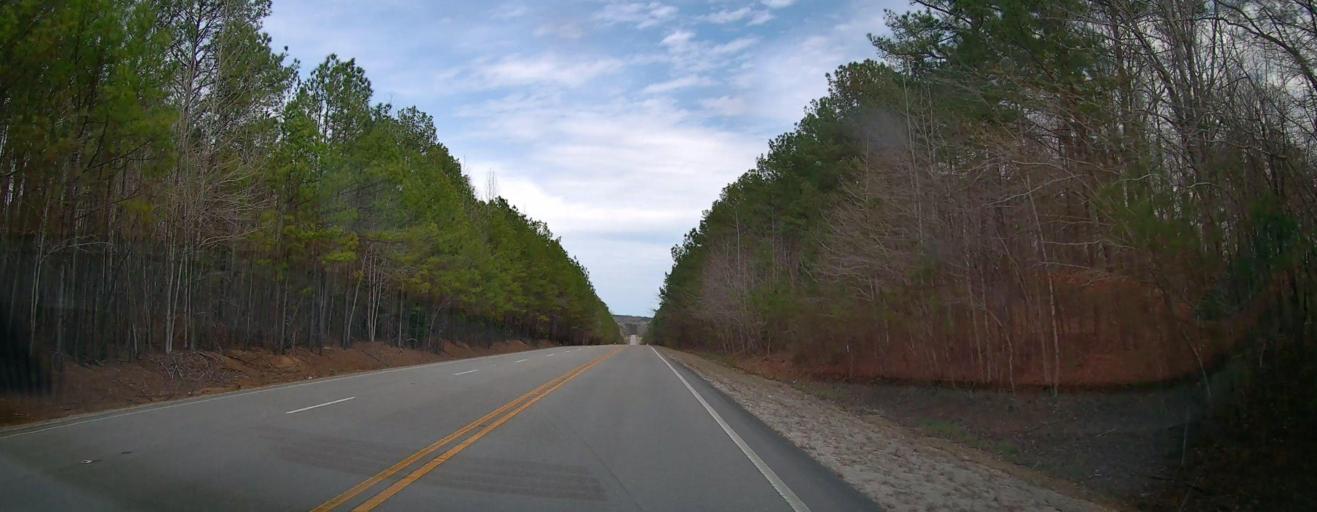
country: US
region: Alabama
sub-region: Marion County
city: Winfield
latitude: 33.9312
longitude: -87.7467
